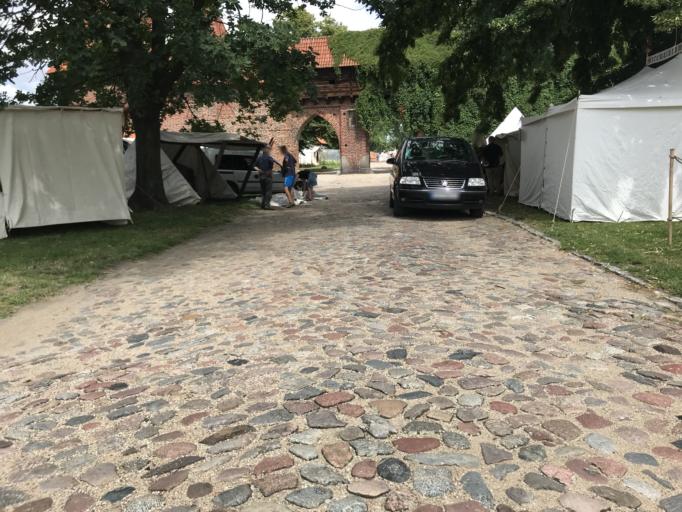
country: PL
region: Pomeranian Voivodeship
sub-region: Powiat malborski
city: Malbork
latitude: 54.0396
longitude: 19.0262
